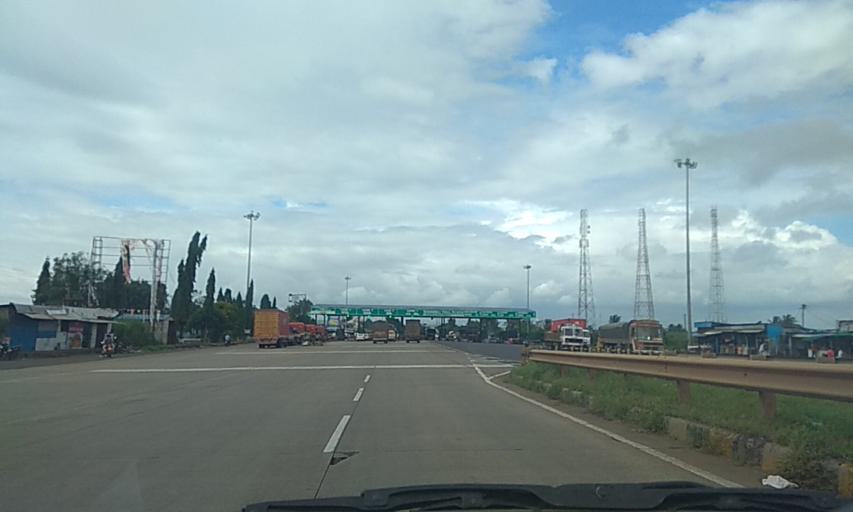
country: IN
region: Maharashtra
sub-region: Kolhapur
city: Kagal
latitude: 16.5407
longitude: 74.3183
